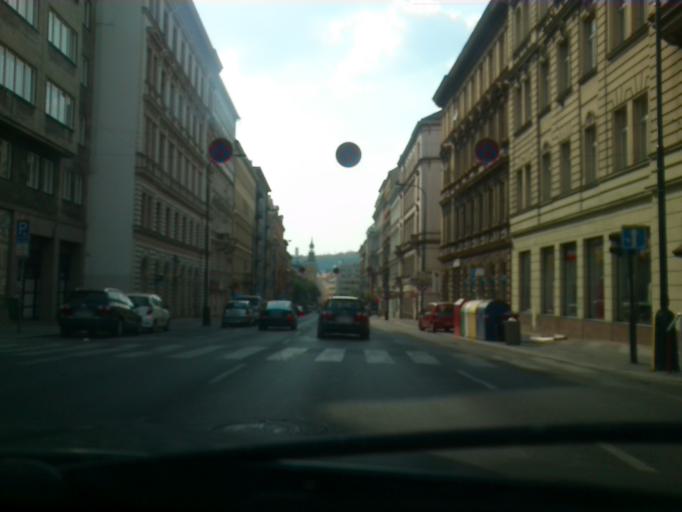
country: CZ
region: Praha
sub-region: Praha 1
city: Stare Mesto
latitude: 50.0774
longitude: 14.4248
